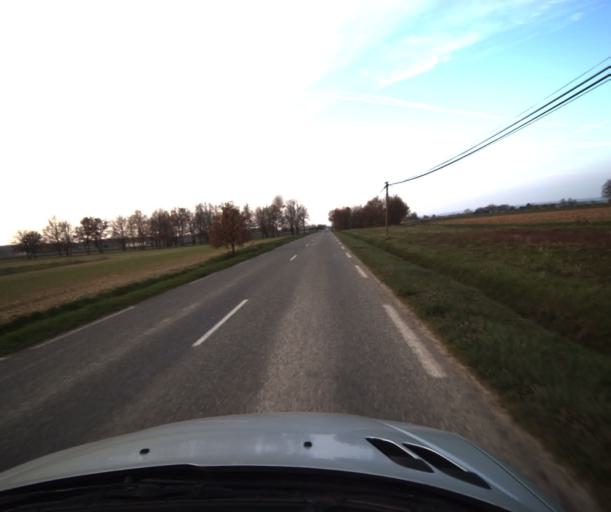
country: FR
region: Midi-Pyrenees
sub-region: Departement de la Haute-Garonne
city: Fronton
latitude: 43.8564
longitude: 1.3848
